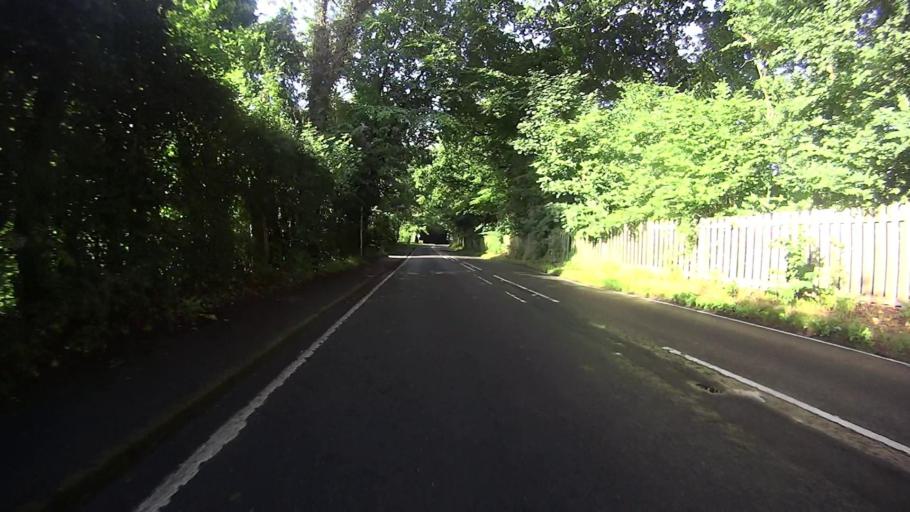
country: GB
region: England
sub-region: Surrey
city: Felbridge
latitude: 51.1437
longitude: -0.0190
